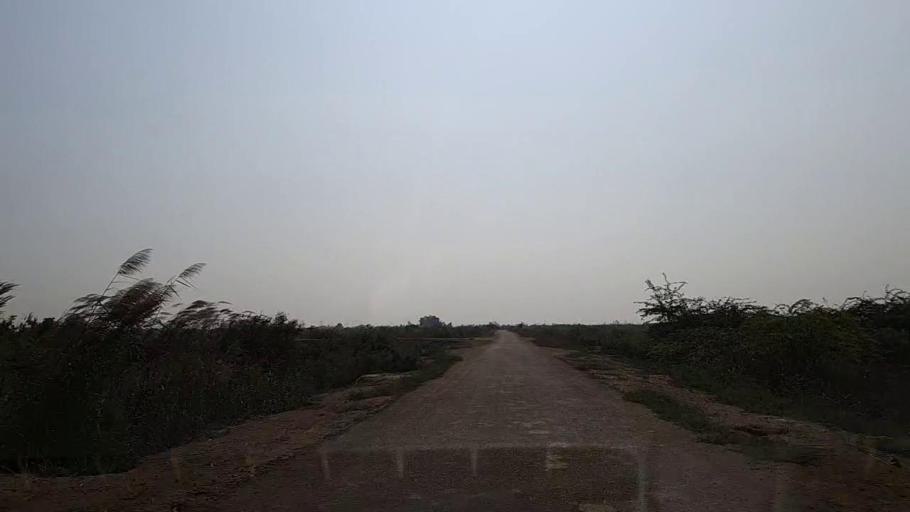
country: PK
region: Sindh
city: Mirpur Sakro
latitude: 24.6555
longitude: 67.6915
